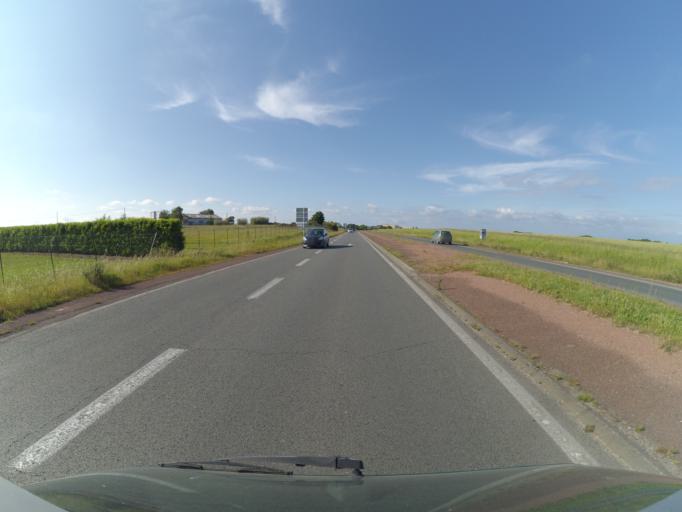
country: FR
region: Poitou-Charentes
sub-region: Departement de la Charente-Maritime
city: Saint-Sulpice-de-Royan
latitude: 45.6796
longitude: -0.9984
